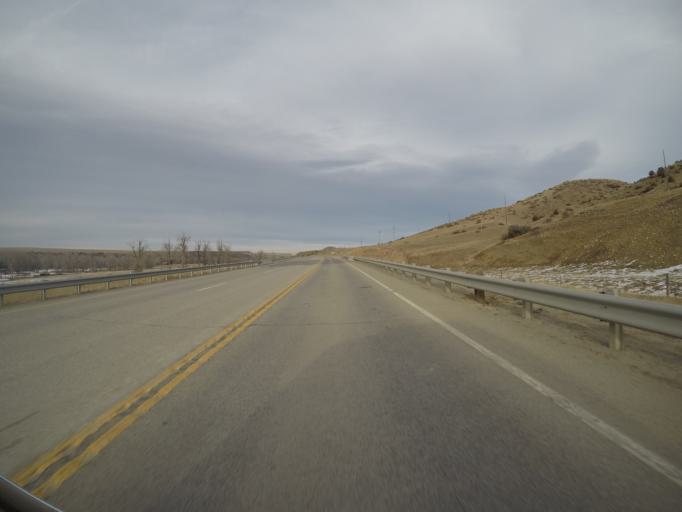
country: US
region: Montana
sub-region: Stillwater County
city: Absarokee
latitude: 45.4951
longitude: -109.4501
